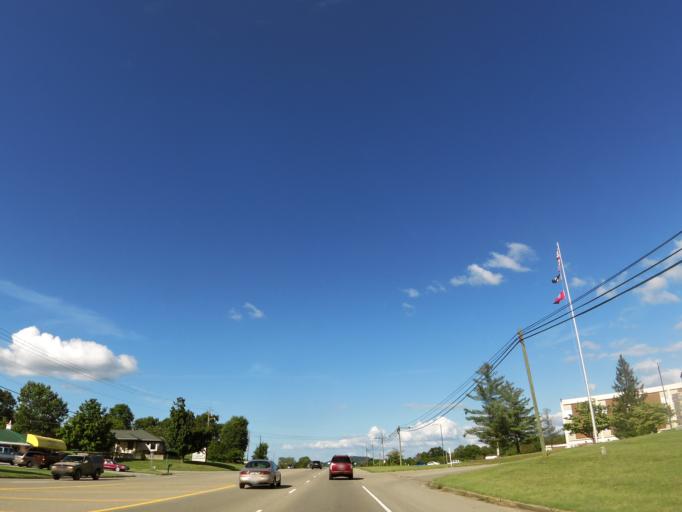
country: US
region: Tennessee
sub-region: Greene County
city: Tusculum
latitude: 36.1845
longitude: -82.7422
